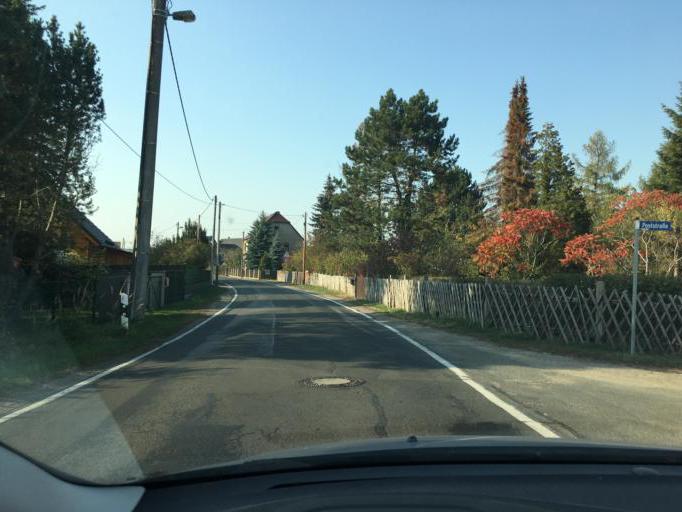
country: DE
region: Saxony
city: Mutzschen
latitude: 51.3143
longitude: 12.8661
